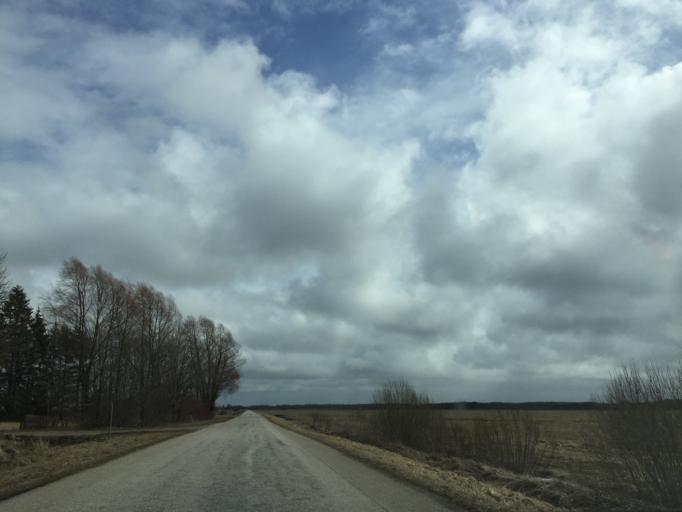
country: EE
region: Laeaene
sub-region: Lihula vald
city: Lihula
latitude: 58.7318
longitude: 23.8738
